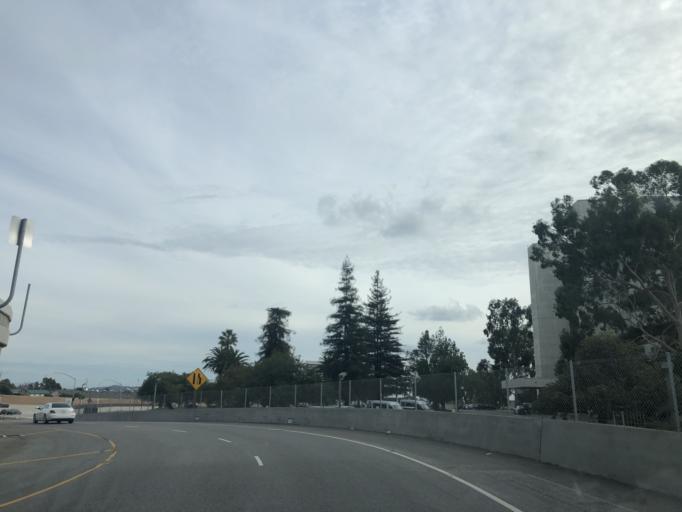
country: US
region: California
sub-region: Los Angeles County
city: Westwood, Los Angeles
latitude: 34.0541
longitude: -118.4524
